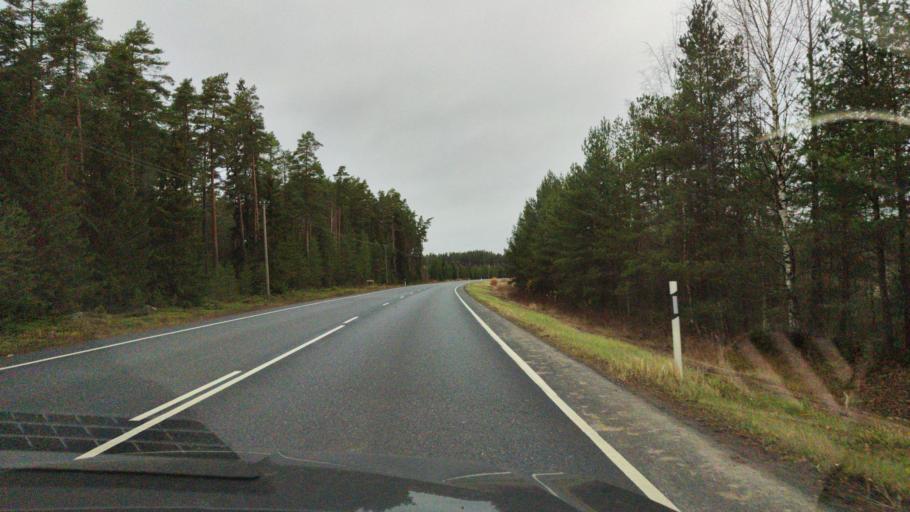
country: FI
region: Satakunta
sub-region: Rauma
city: Eura
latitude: 61.1218
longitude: 22.1803
